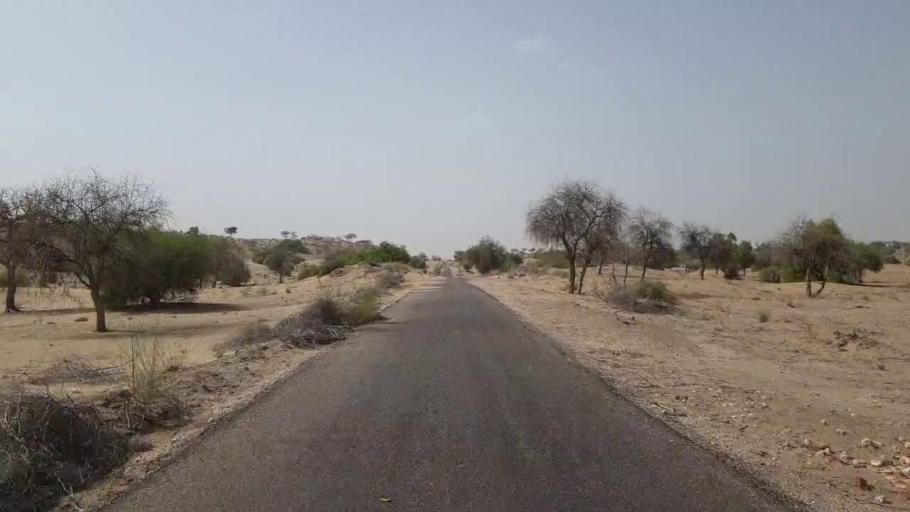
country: PK
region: Sindh
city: Mithi
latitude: 24.5839
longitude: 69.9228
